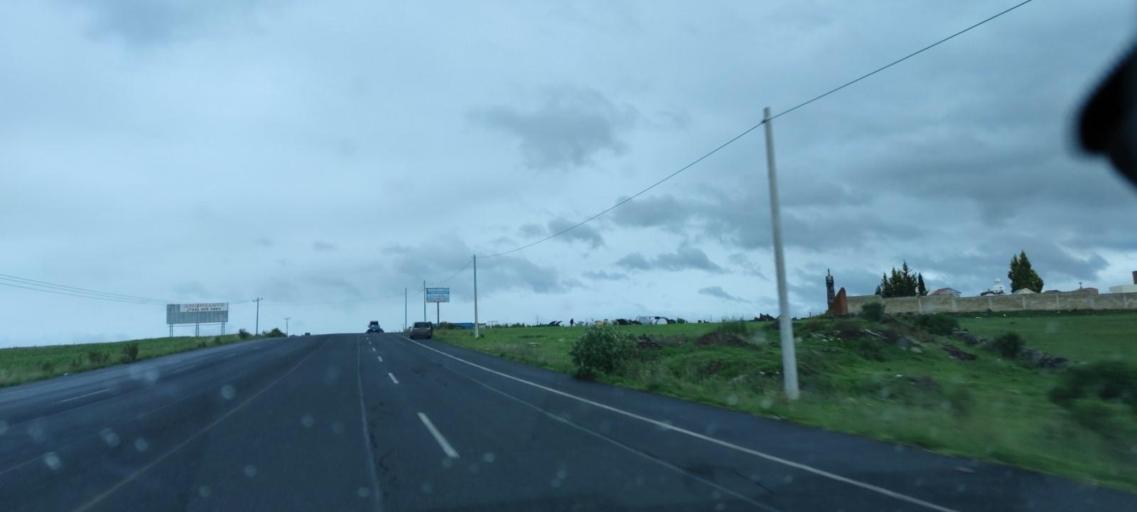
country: MX
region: Mexico
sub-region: Jilotepec
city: Octeyuco Dos Mil
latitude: 19.8851
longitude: -99.6510
